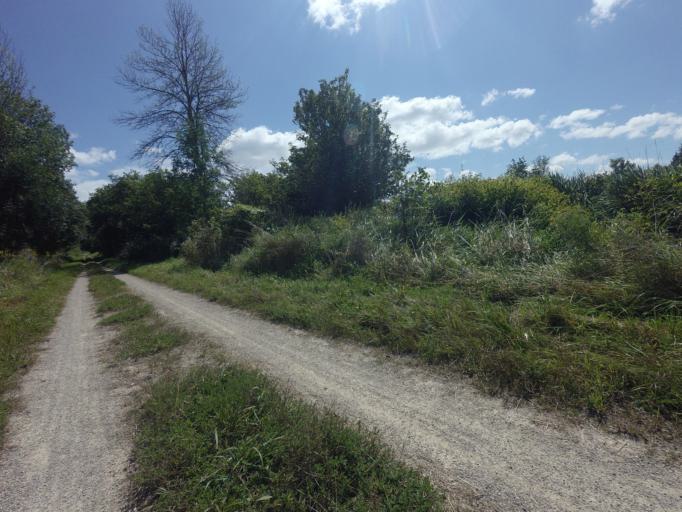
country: CA
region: Ontario
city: Orangeville
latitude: 43.7914
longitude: -80.2930
